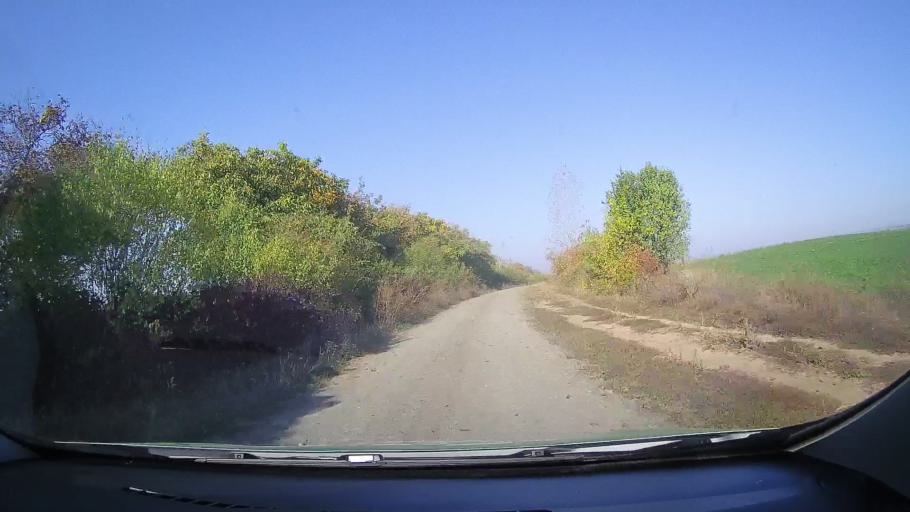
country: RO
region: Satu Mare
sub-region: Comuna Sauca
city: Sauca
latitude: 47.4735
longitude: 22.4818
